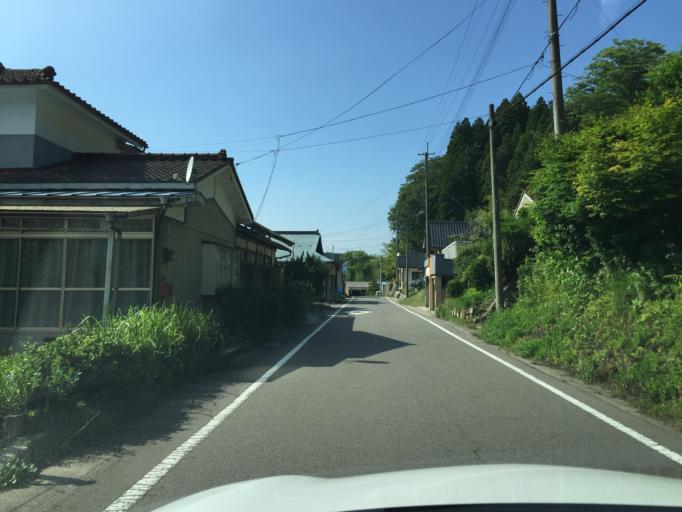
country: JP
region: Fukushima
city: Ishikawa
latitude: 37.1826
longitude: 140.6243
